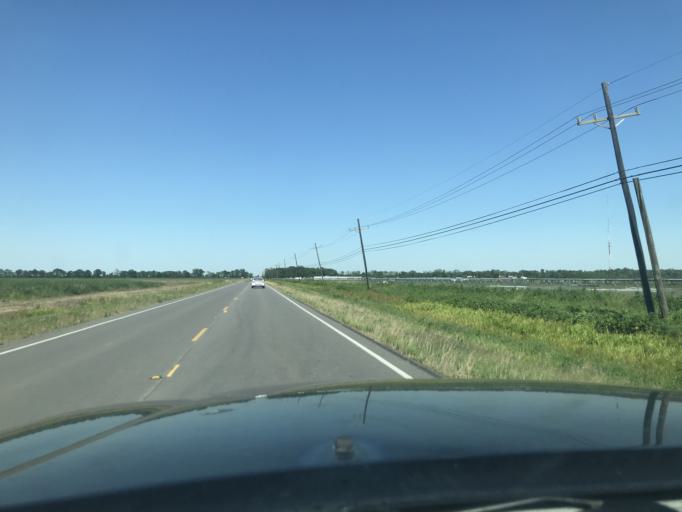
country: US
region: Louisiana
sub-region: West Baton Rouge Parish
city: Erwinville
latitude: 30.4686
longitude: -91.3356
